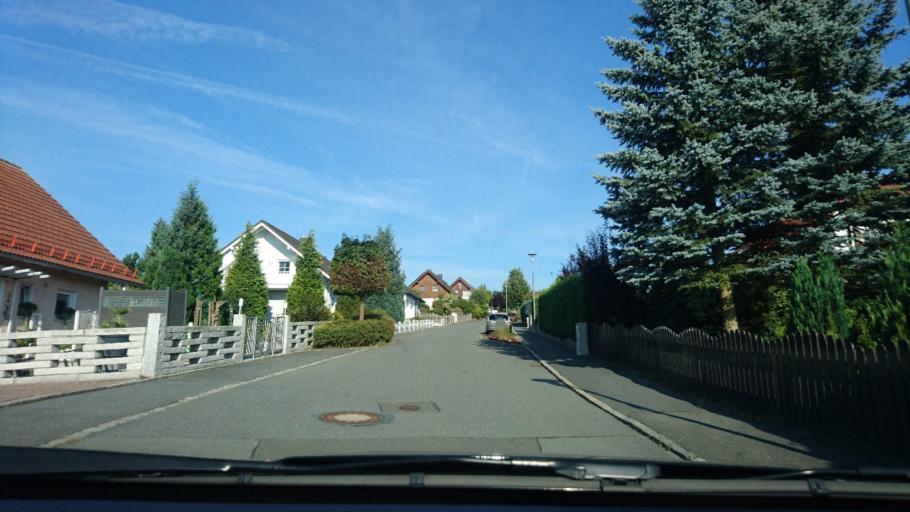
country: DE
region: Bavaria
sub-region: Upper Franconia
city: Naila
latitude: 50.3336
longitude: 11.6958
